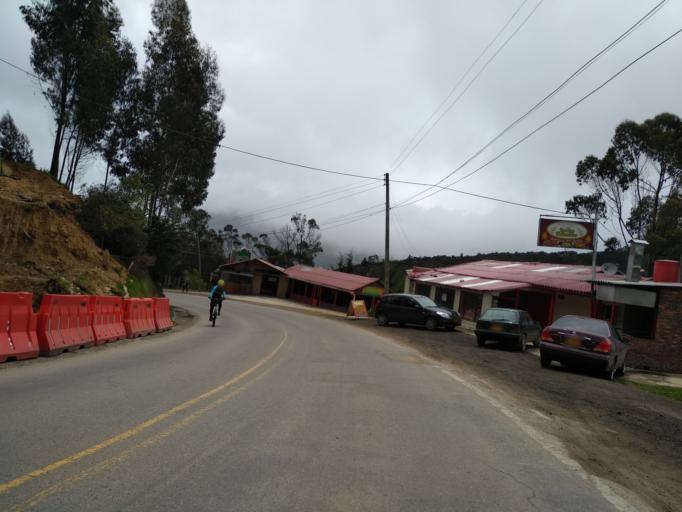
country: CO
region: Bogota D.C.
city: Barrio San Luis
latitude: 4.6621
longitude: -74.0041
